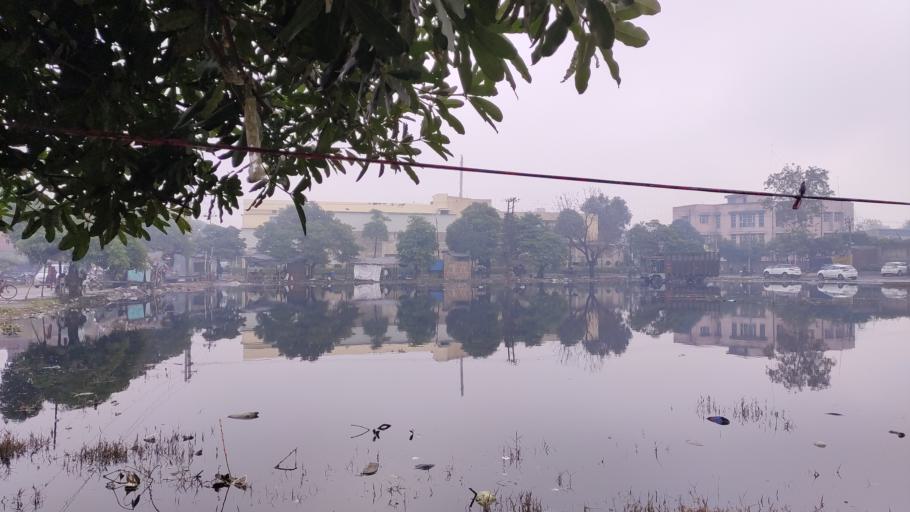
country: IN
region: Punjab
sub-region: Amritsar
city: Amritsar
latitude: 31.6196
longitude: 74.9164
